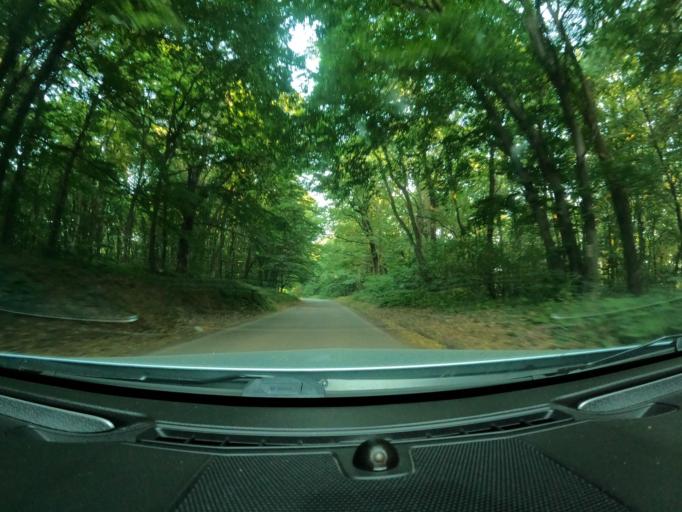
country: RS
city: Vrdnik
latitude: 45.1610
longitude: 19.7605
